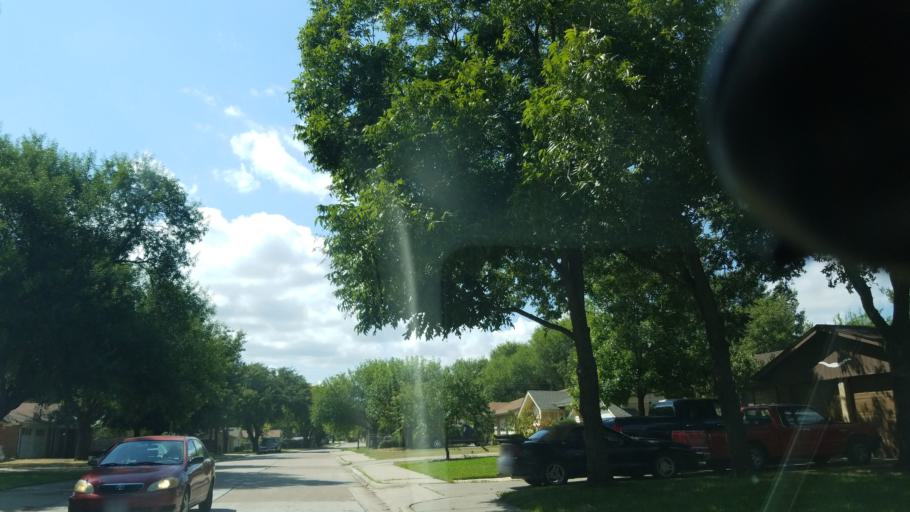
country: US
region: Texas
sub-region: Dallas County
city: Grand Prairie
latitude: 32.7198
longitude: -96.9985
